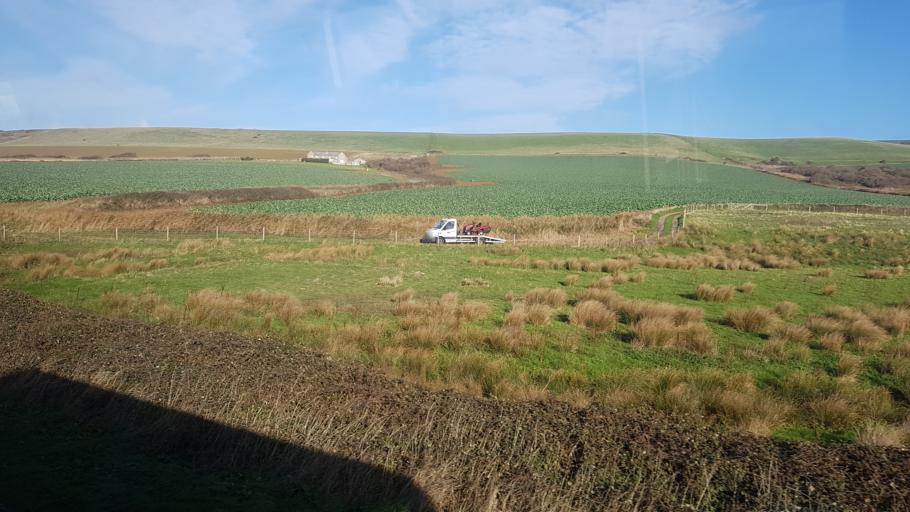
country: GB
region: England
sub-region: Isle of Wight
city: Freshwater
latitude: 50.6550
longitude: -1.4658
